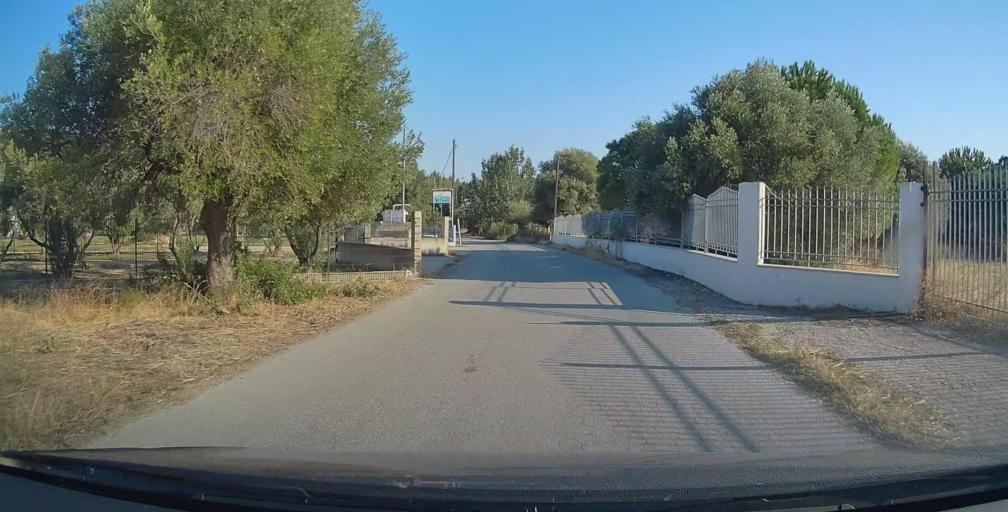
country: GR
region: Central Macedonia
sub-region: Nomos Chalkidikis
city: Sykia
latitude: 39.9969
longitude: 23.8896
